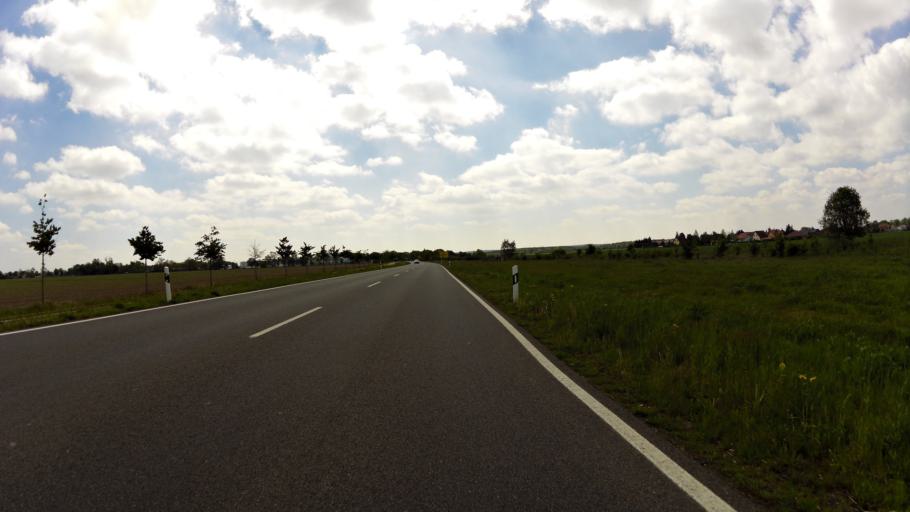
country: DE
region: Saxony
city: Torgau
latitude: 51.5184
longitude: 13.0349
